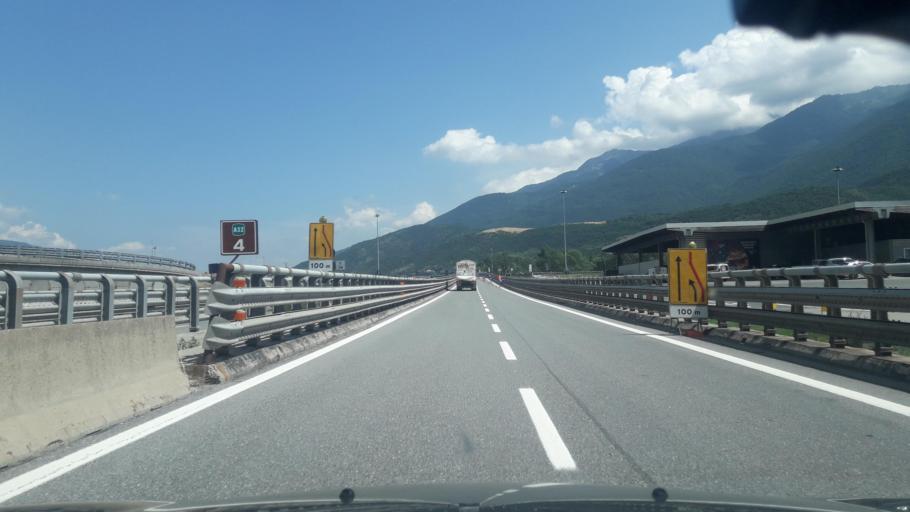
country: IT
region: Piedmont
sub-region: Provincia di Torino
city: Susa
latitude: 45.1367
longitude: 7.0749
